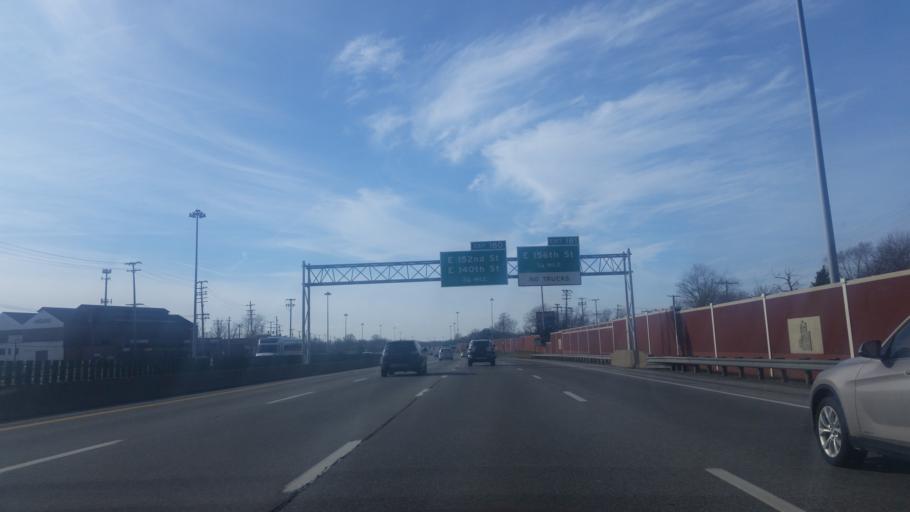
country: US
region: Ohio
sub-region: Cuyahoga County
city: East Cleveland
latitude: 41.5716
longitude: -81.5651
